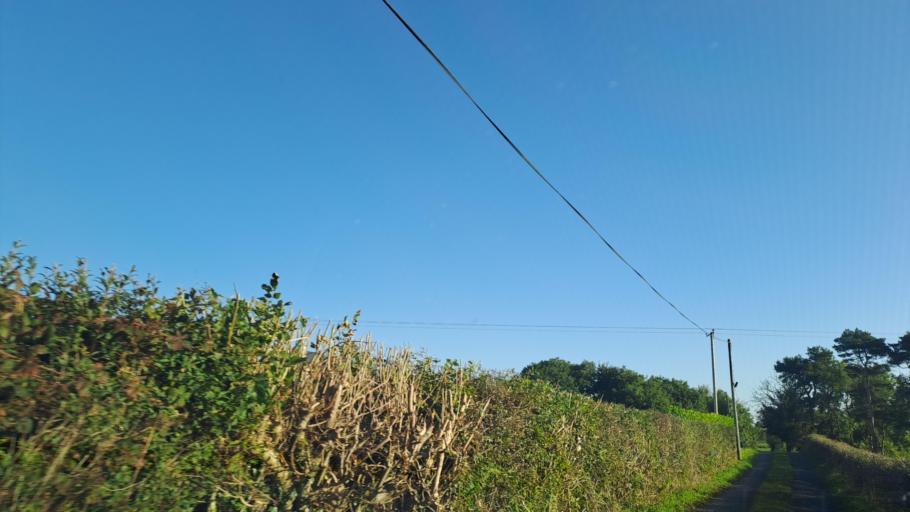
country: IE
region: Ulster
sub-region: An Cabhan
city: Kingscourt
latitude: 53.9817
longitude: -6.8363
